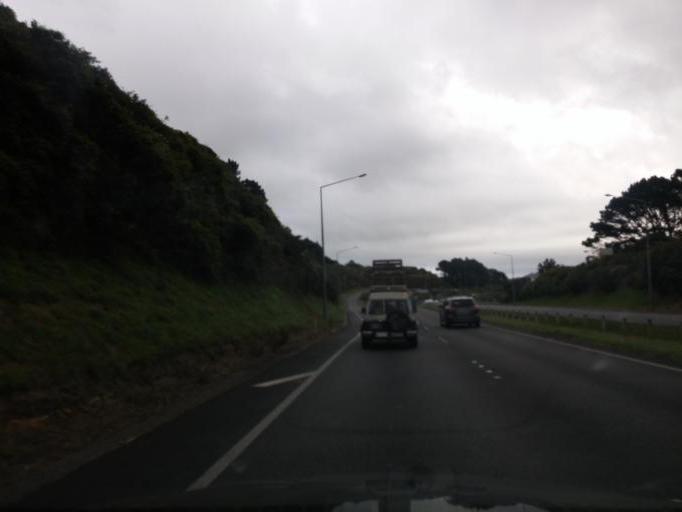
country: NZ
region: Wellington
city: Petone
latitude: -41.2010
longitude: 174.8236
